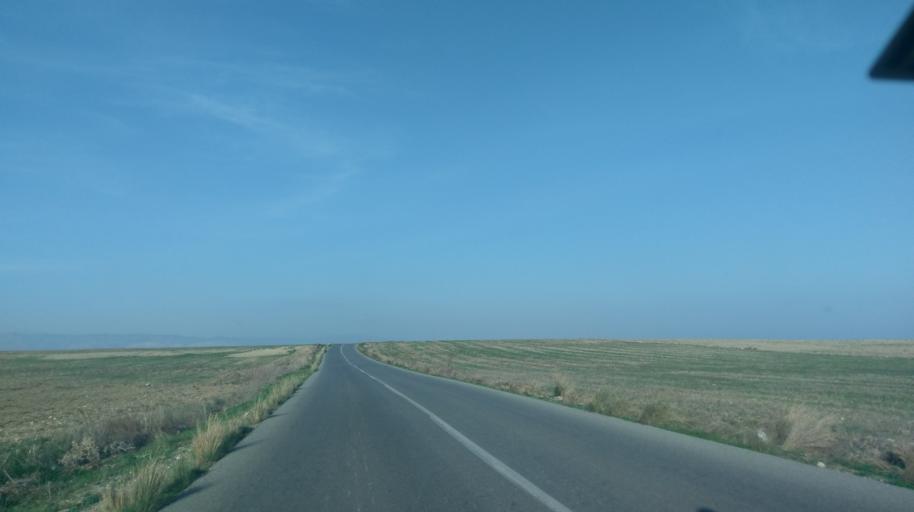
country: CY
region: Ammochostos
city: Achna
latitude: 35.1389
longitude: 33.7435
